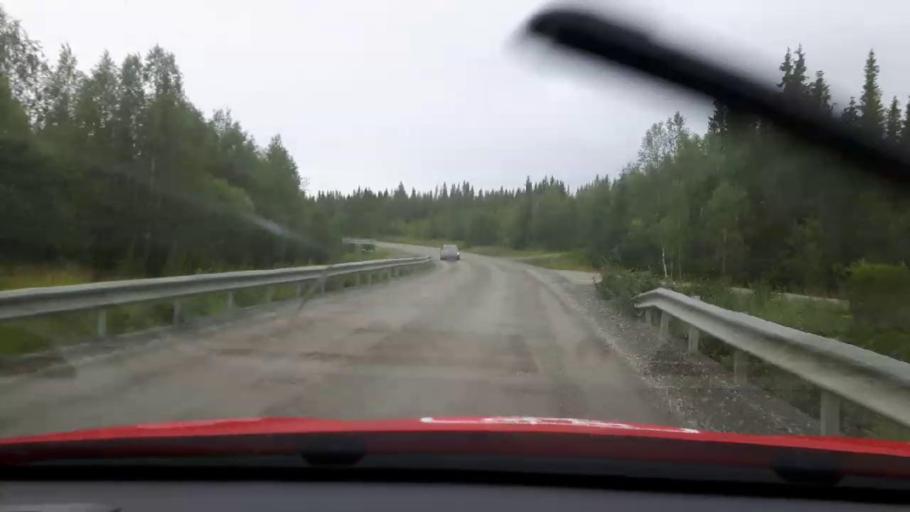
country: SE
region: Jaemtland
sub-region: Are Kommun
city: Are
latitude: 63.4440
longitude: 12.6932
